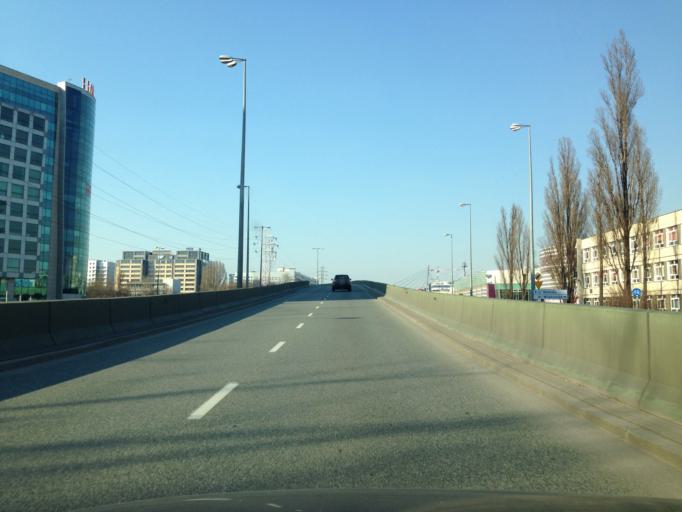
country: PL
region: Masovian Voivodeship
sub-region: Warszawa
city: Mokotow
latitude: 52.1766
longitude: 21.0024
